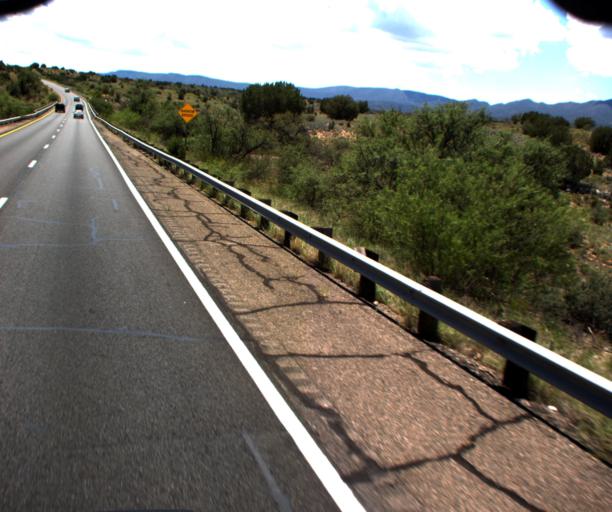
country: US
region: Arizona
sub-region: Yavapai County
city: Verde Village
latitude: 34.6699
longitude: -111.9704
